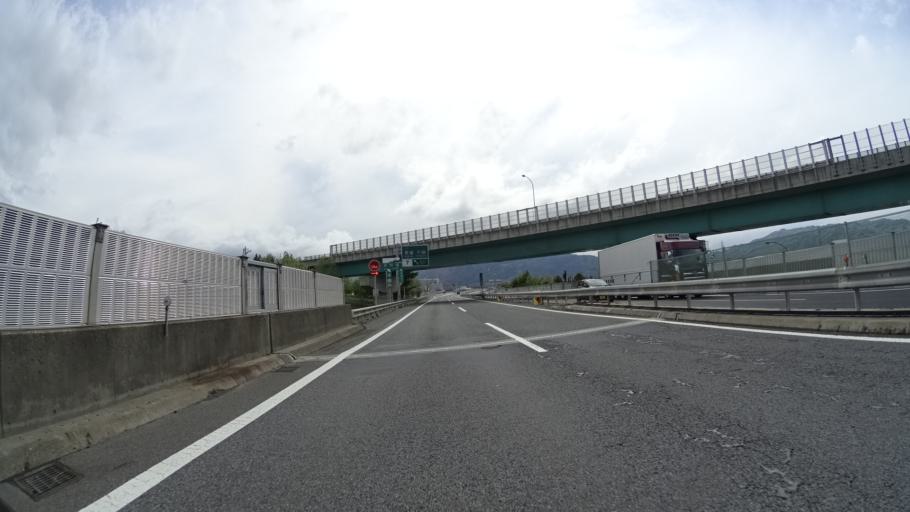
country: JP
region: Nagano
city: Nagano-shi
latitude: 36.5529
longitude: 138.1421
